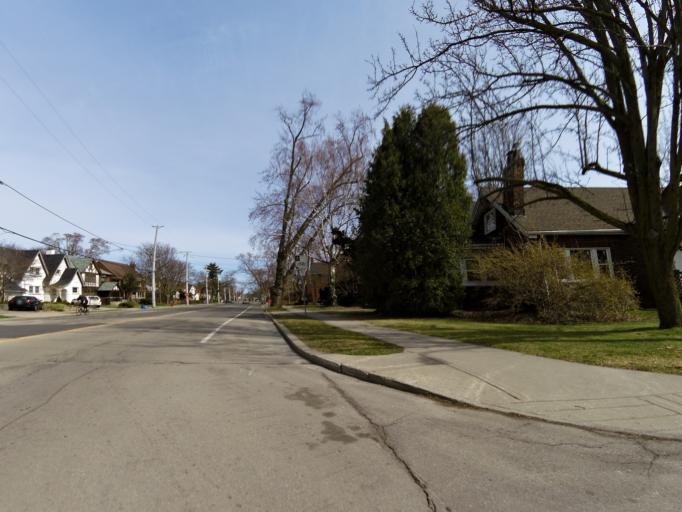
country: CA
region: Ontario
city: Hamilton
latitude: 43.2621
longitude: -79.9134
